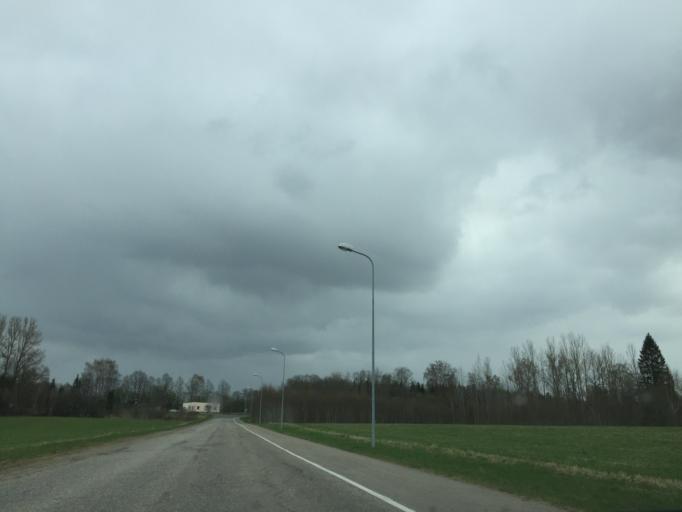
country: LV
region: Priekuli
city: Priekuli
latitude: 57.3458
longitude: 25.3360
